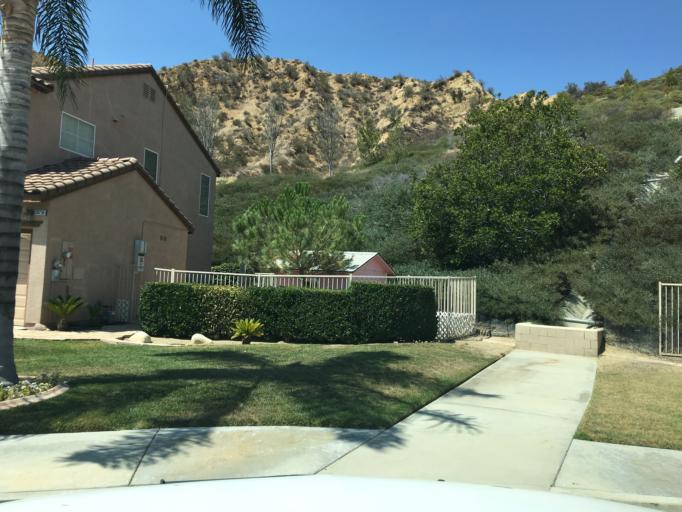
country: US
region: California
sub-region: Los Angeles County
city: Castaic
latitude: 34.4689
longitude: -118.6303
